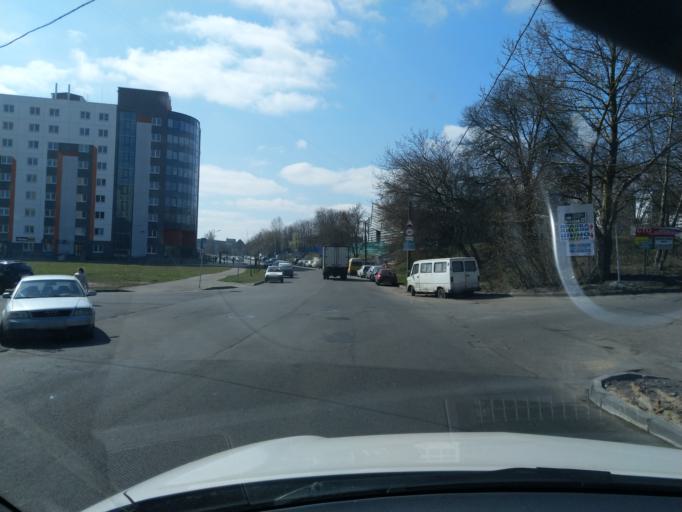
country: BY
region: Minsk
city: Syenitsa
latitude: 53.8683
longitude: 27.5098
